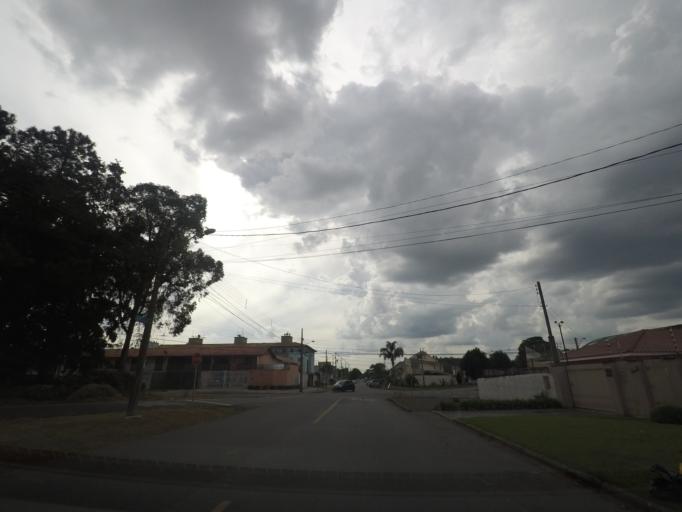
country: BR
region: Parana
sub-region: Sao Jose Dos Pinhais
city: Sao Jose dos Pinhais
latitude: -25.4896
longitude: -49.2460
